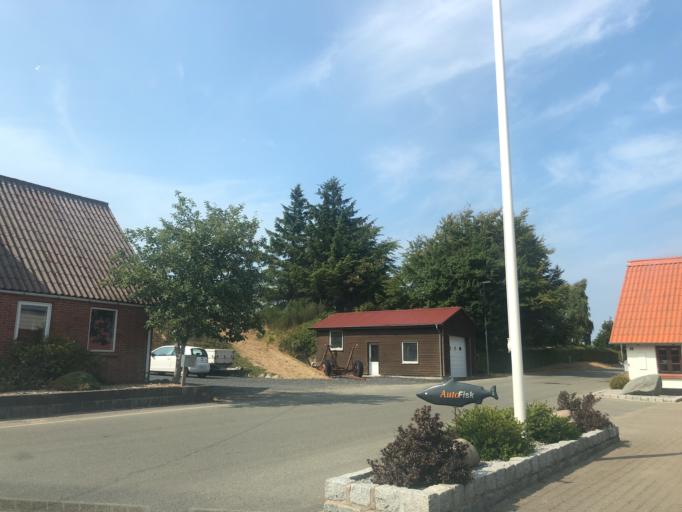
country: DK
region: North Denmark
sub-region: Morso Kommune
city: Nykobing Mors
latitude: 56.8184
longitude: 9.0287
